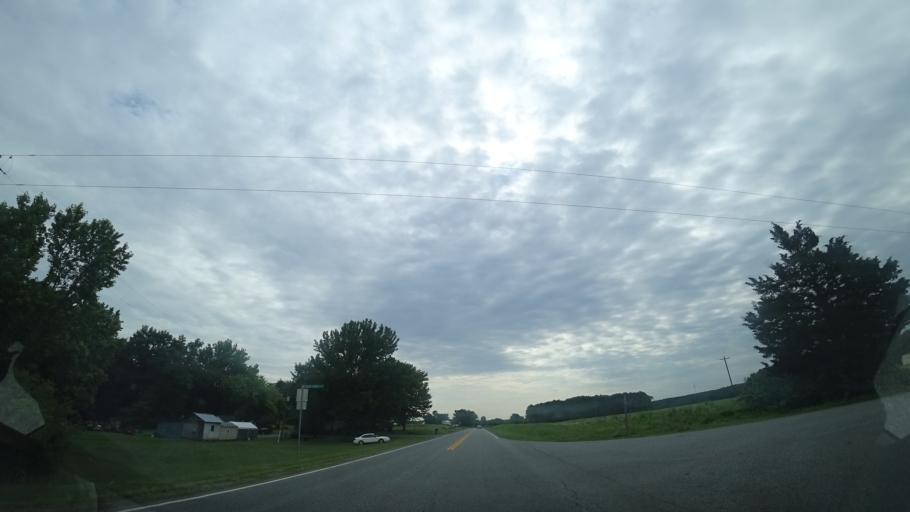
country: US
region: Virginia
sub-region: Spotsylvania County
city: Spotsylvania
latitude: 38.1476
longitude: -77.7120
